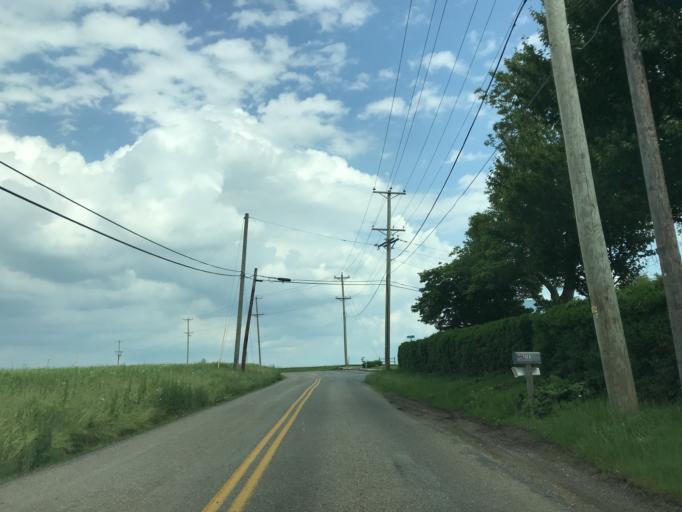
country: US
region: Pennsylvania
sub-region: York County
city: Susquehanna Trails
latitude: 39.6665
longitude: -76.3736
